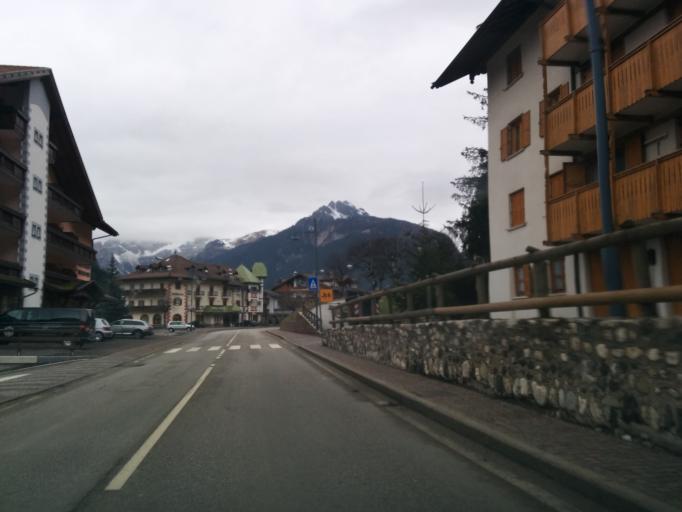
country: IT
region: Trentino-Alto Adige
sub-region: Provincia di Trento
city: Canazei
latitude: 46.4774
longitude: 11.7673
